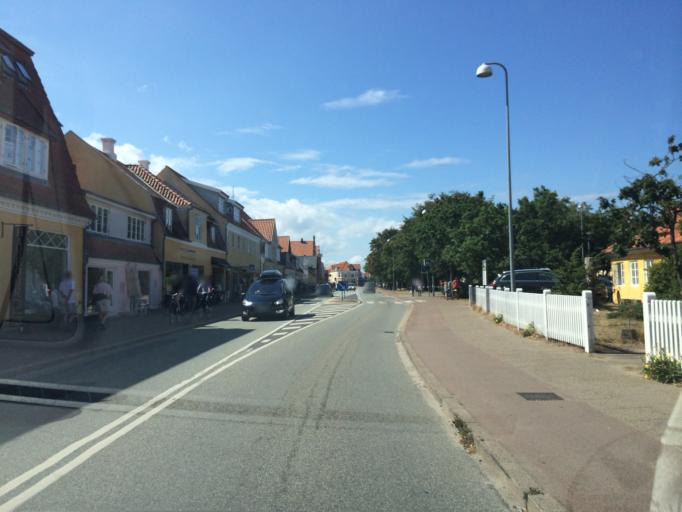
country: DK
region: North Denmark
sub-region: Frederikshavn Kommune
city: Skagen
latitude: 57.7245
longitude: 10.5954
